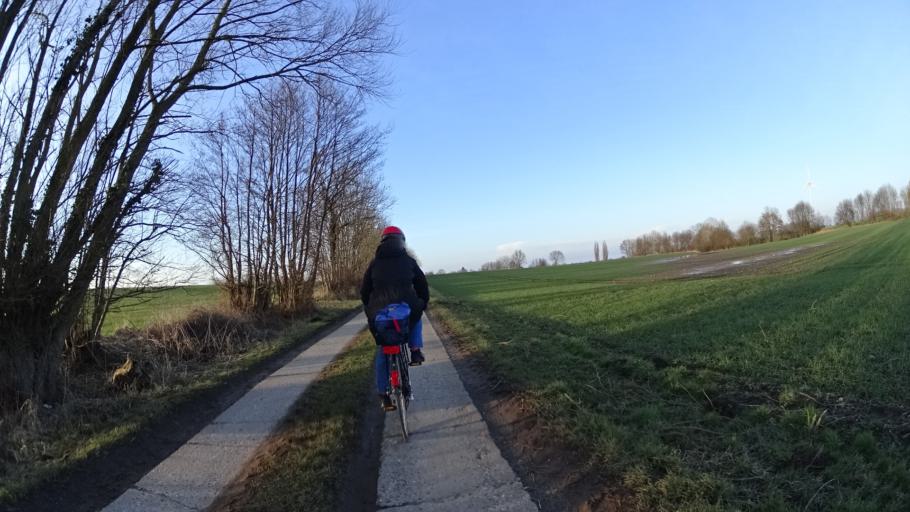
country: DE
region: Schleswig-Holstein
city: Stakendorf
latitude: 54.3816
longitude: 10.4272
